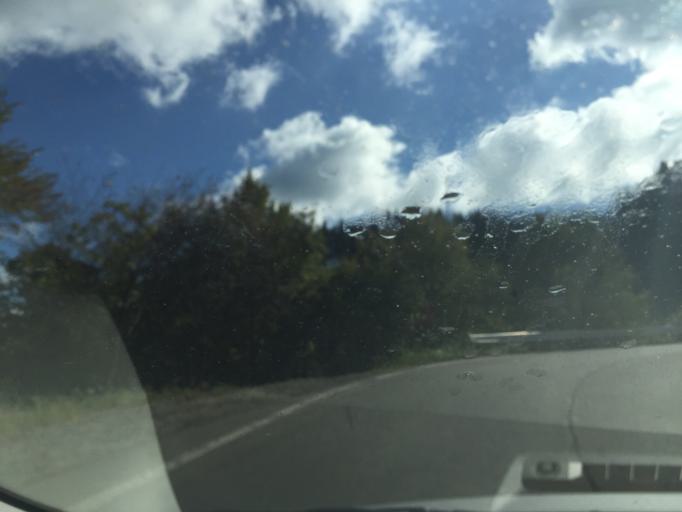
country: JP
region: Gifu
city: Nakatsugawa
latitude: 35.2991
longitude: 137.6734
